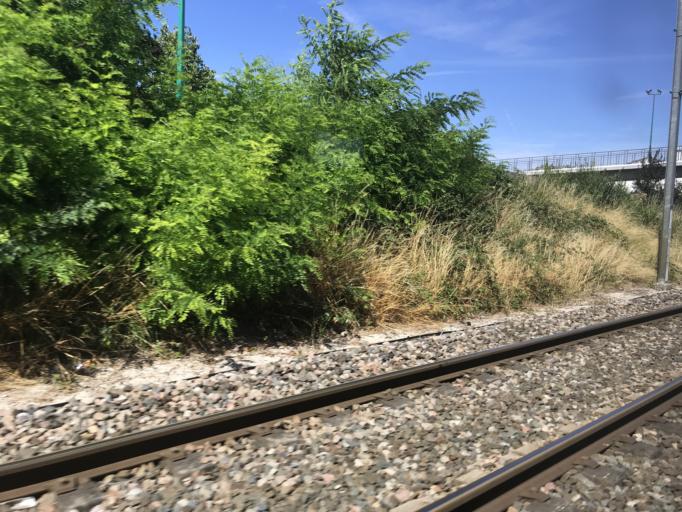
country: FR
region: Champagne-Ardenne
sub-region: Departement de la Marne
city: Reims
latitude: 49.2362
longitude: 4.0201
